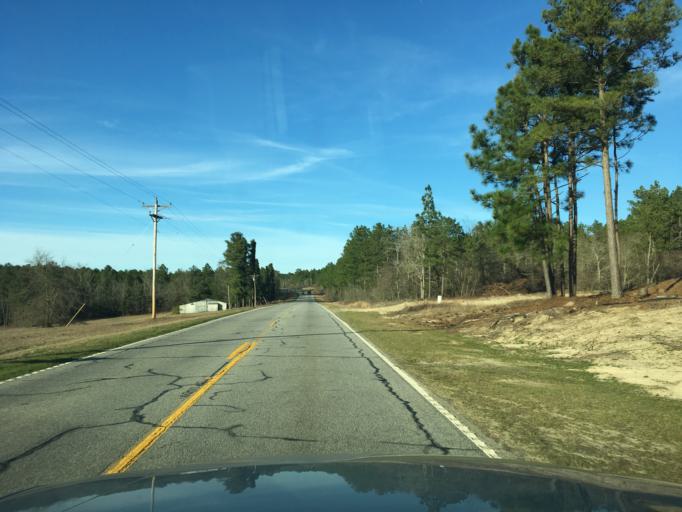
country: US
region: South Carolina
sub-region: Edgefield County
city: Johnston
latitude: 33.7405
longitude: -81.6463
